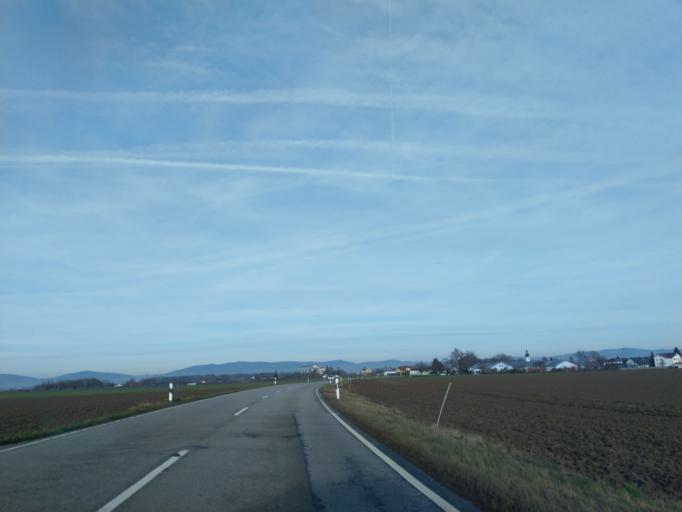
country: DE
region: Bavaria
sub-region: Lower Bavaria
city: Buchhofen
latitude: 48.6915
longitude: 12.9142
